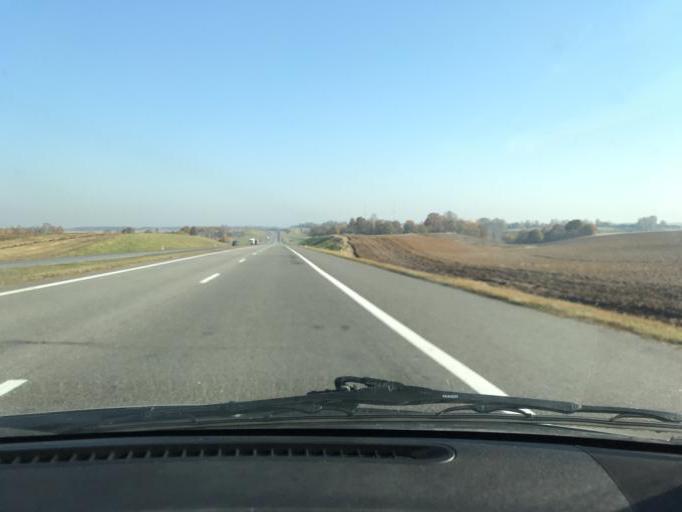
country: BY
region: Vitebsk
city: Baran'
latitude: 54.5644
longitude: 30.2955
